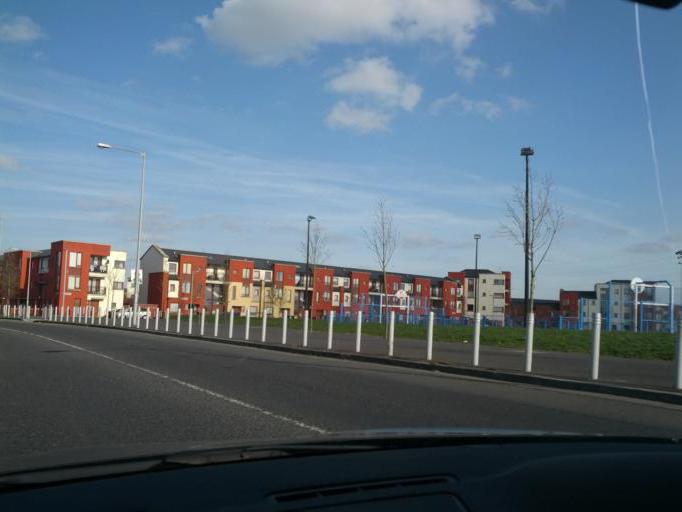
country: IE
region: Leinster
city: Clondalkin
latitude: 53.3394
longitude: -6.4169
